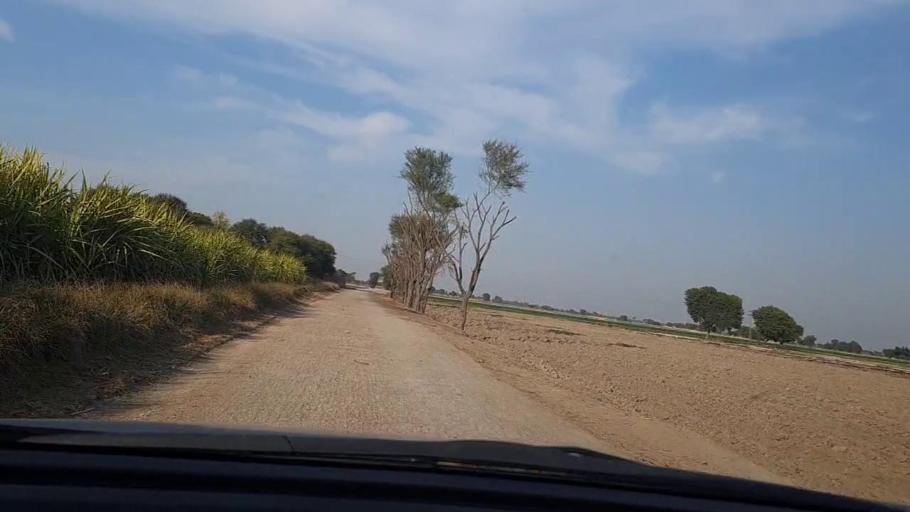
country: PK
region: Sindh
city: Daulatpur
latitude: 26.3339
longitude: 68.0296
